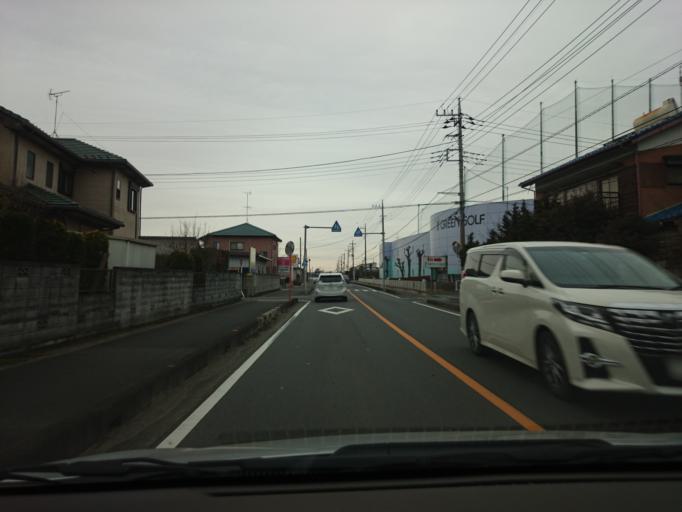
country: JP
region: Saitama
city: Kazo
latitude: 36.1067
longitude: 139.5948
